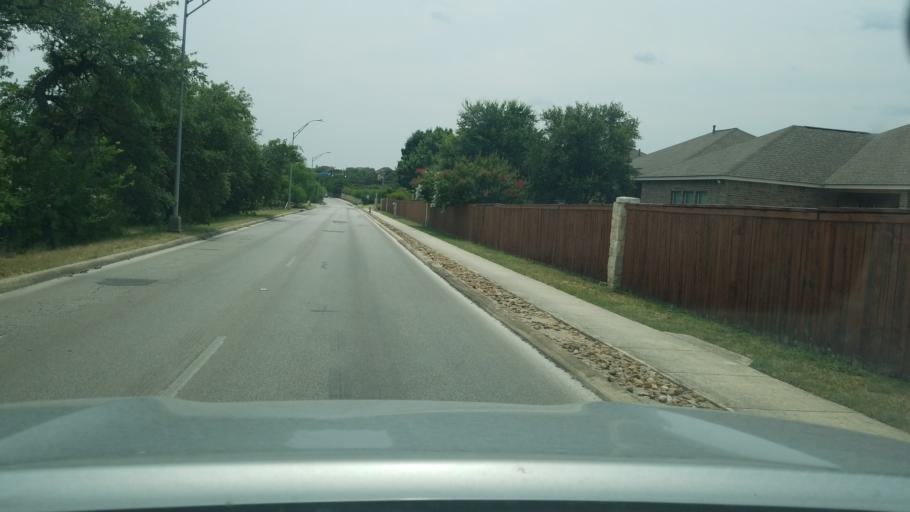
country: US
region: Texas
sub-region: Bexar County
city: Hollywood Park
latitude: 29.6466
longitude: -98.4340
